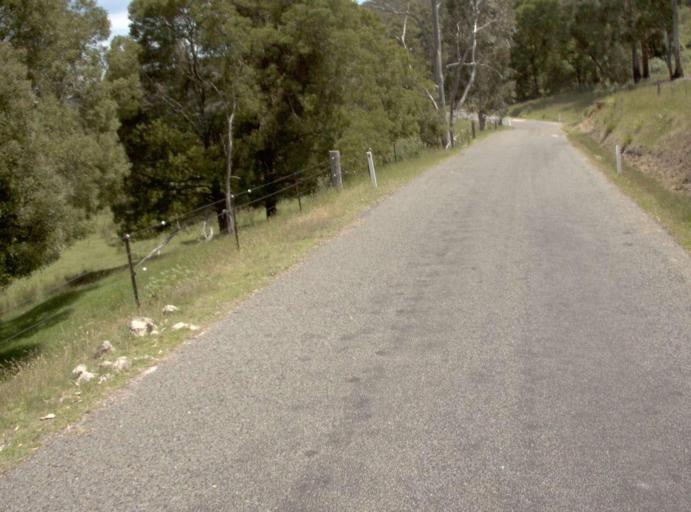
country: AU
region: New South Wales
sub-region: Bombala
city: Bombala
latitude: -37.3609
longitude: 149.0211
